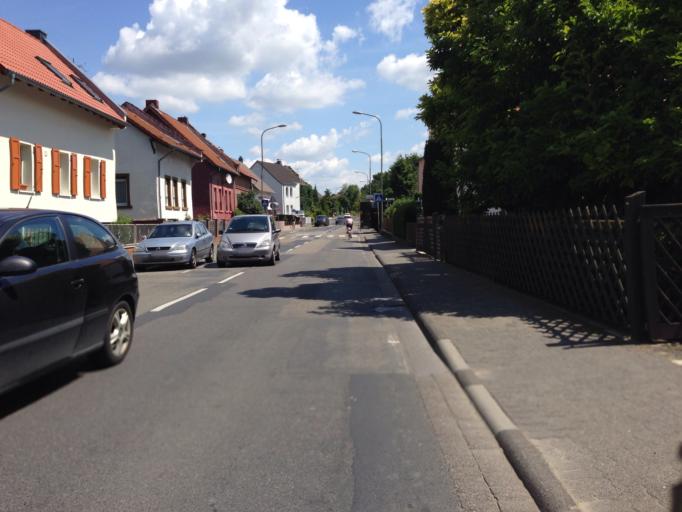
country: DE
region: Hesse
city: Bruchkobel
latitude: 50.1780
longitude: 8.8925
